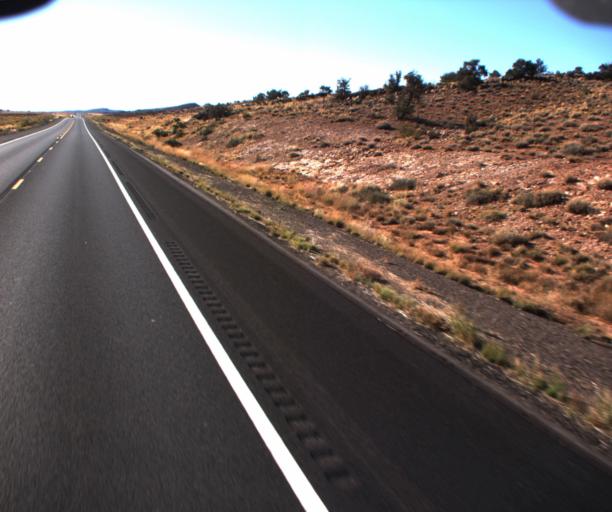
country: US
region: Arizona
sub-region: Coconino County
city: LeChee
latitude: 36.5032
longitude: -111.5827
